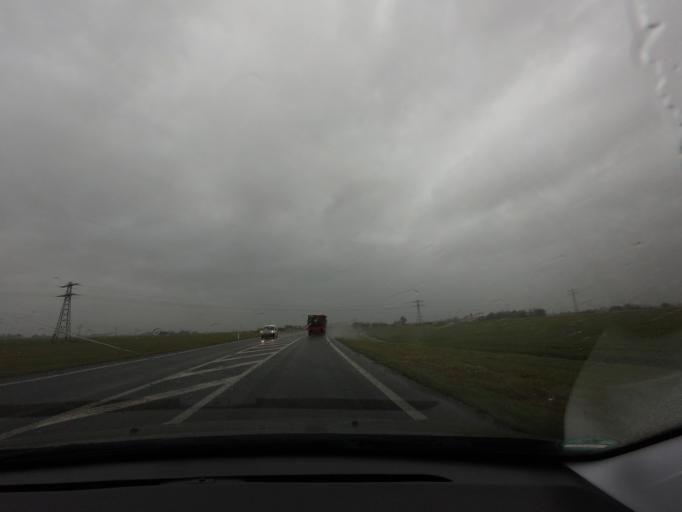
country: NL
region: Friesland
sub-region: Sudwest Fryslan
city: Bolsward
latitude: 53.0743
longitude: 5.5110
